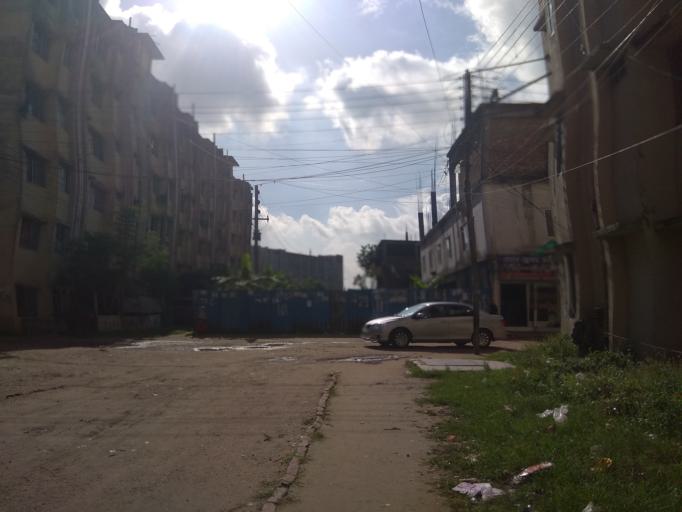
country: BD
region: Dhaka
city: Paltan
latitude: 23.8067
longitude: 90.3877
